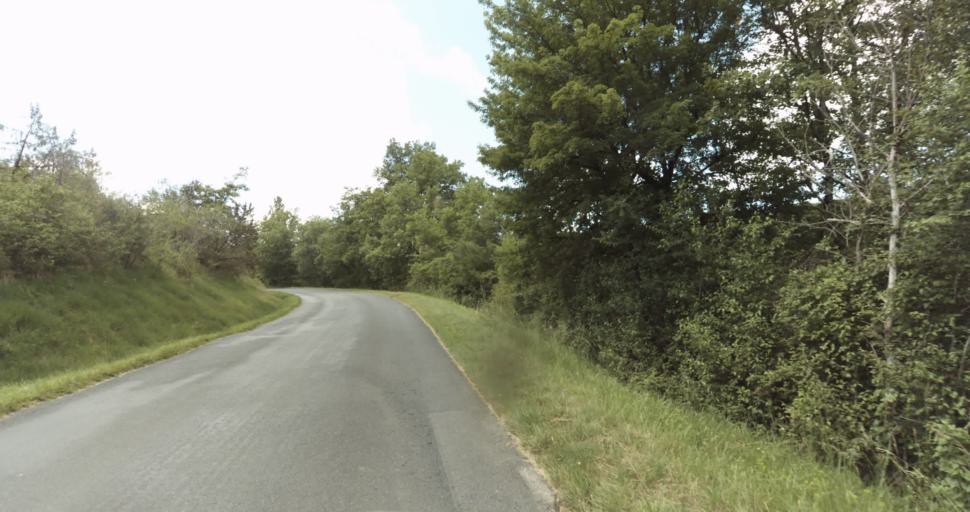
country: FR
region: Aquitaine
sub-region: Departement de la Dordogne
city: Beaumont-du-Perigord
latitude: 44.7645
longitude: 0.7409
